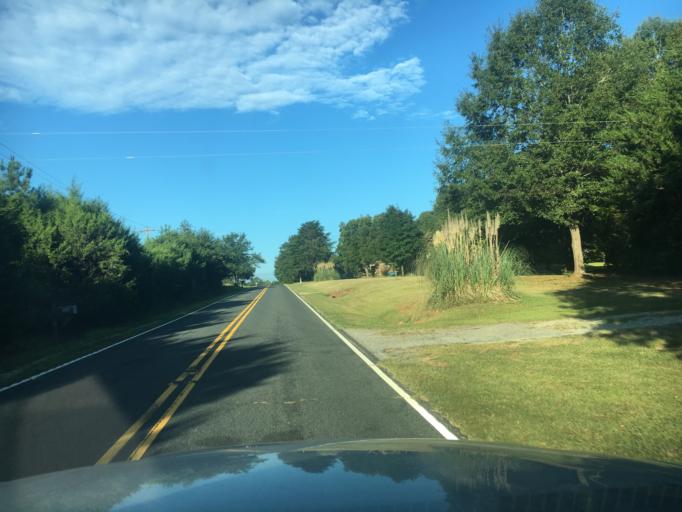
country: US
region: South Carolina
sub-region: Spartanburg County
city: Woodruff
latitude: 34.6227
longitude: -82.0725
